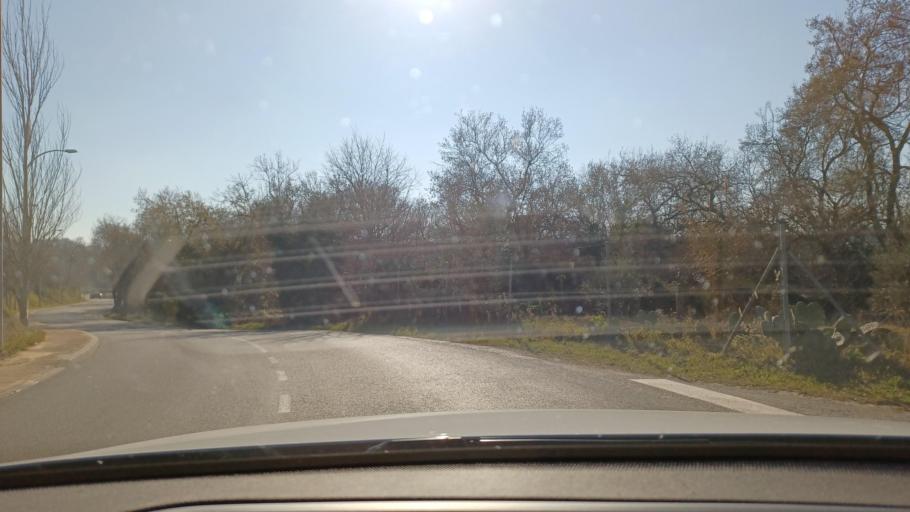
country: ES
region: Catalonia
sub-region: Provincia de Barcelona
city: Vilobi del Penedes
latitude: 41.3638
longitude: 1.6702
